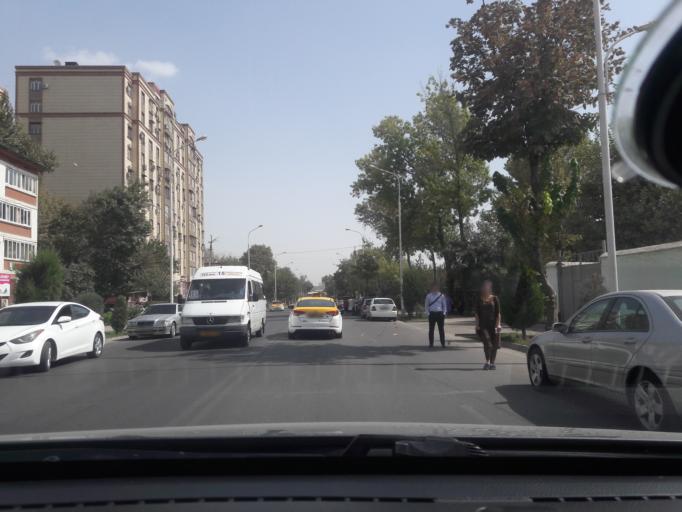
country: TJ
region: Dushanbe
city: Dushanbe
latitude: 38.5641
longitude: 68.7574
